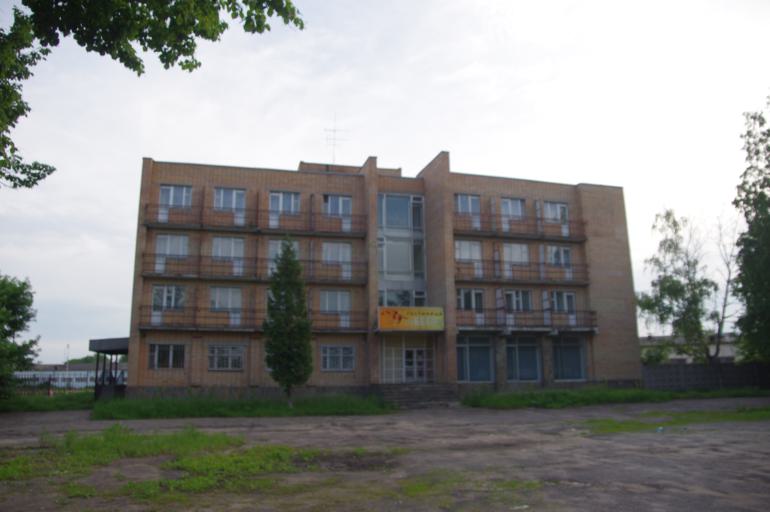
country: RU
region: Moskovskaya
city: Ramenskoye
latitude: 55.5573
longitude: 38.2388
